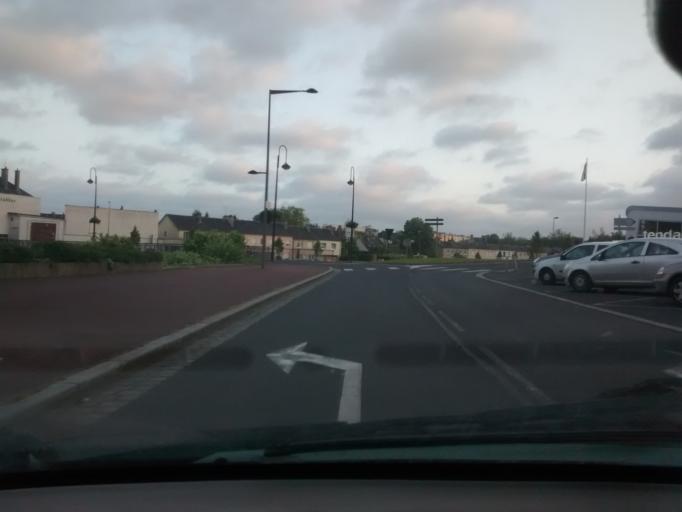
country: FR
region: Lower Normandy
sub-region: Departement de la Manche
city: Agneaux
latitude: 49.1158
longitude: -1.0997
